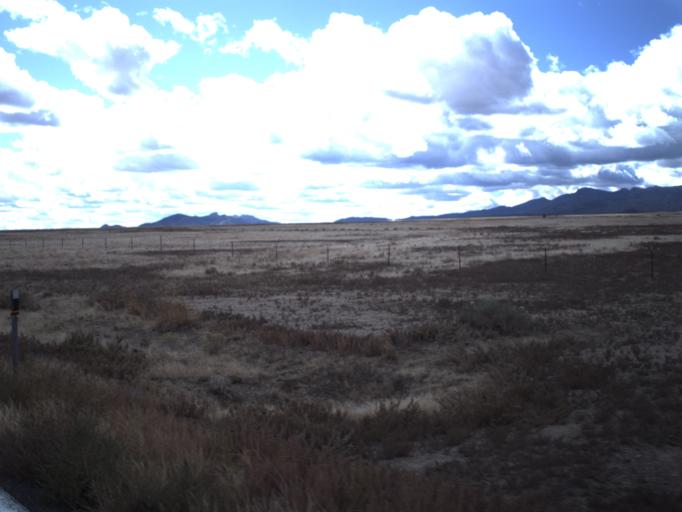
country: US
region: Utah
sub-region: Beaver County
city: Milford
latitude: 38.6584
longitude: -113.8752
